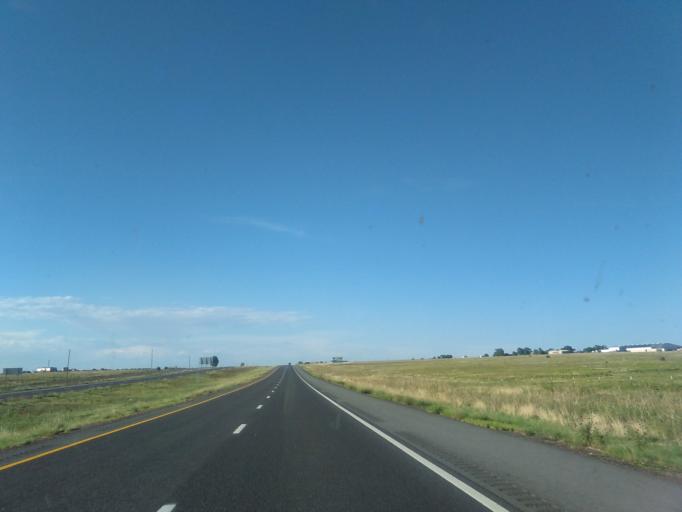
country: US
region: New Mexico
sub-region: San Miguel County
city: Las Vegas
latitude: 35.6456
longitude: -105.1943
